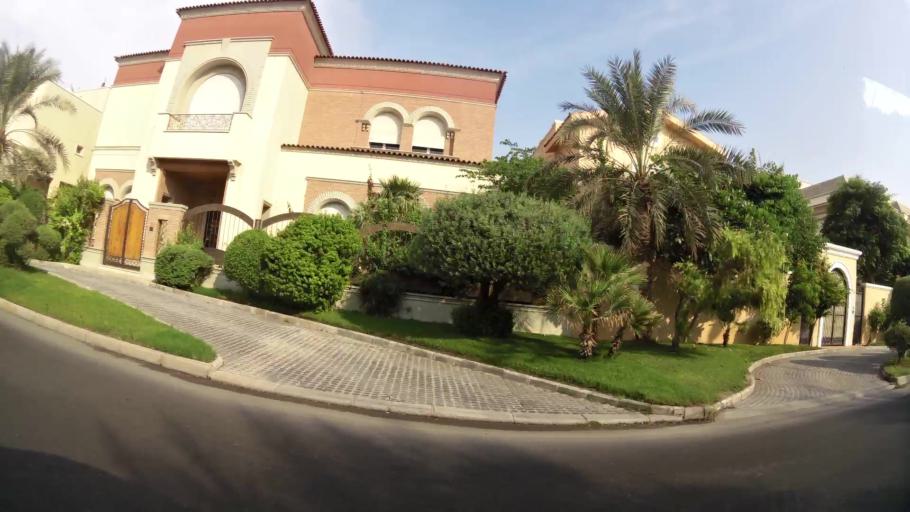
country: KW
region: Al Farwaniyah
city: Janub as Surrah
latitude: 29.3111
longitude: 47.9889
